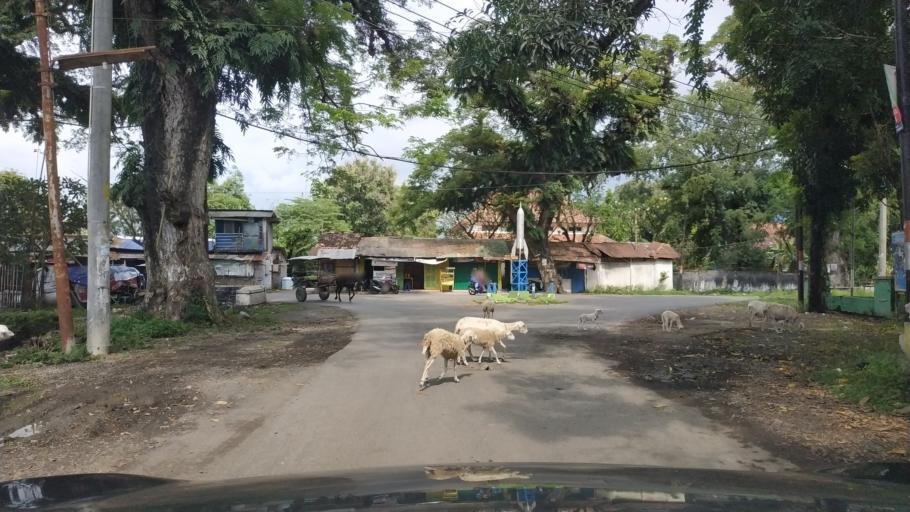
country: ID
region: Central Java
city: Pemalang
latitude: -6.9283
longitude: 109.3397
